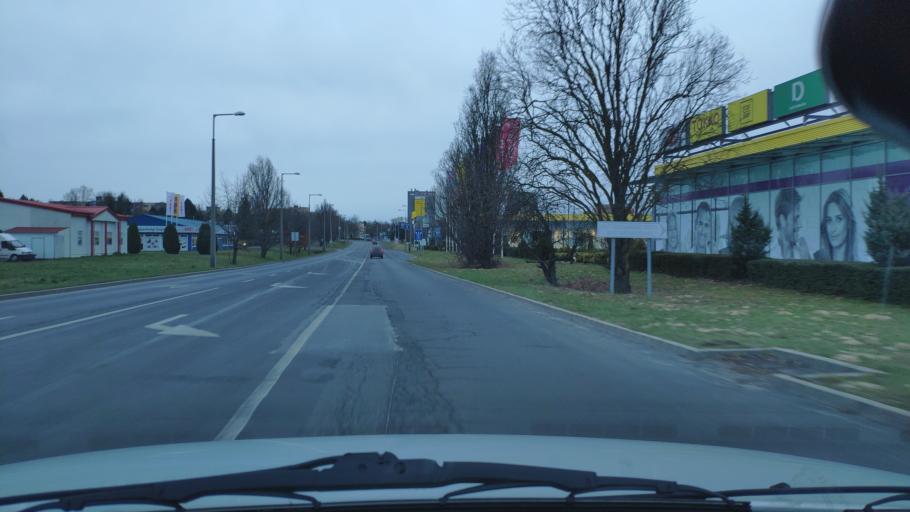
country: HU
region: Zala
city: Nagykanizsa
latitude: 46.4646
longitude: 17.0081
